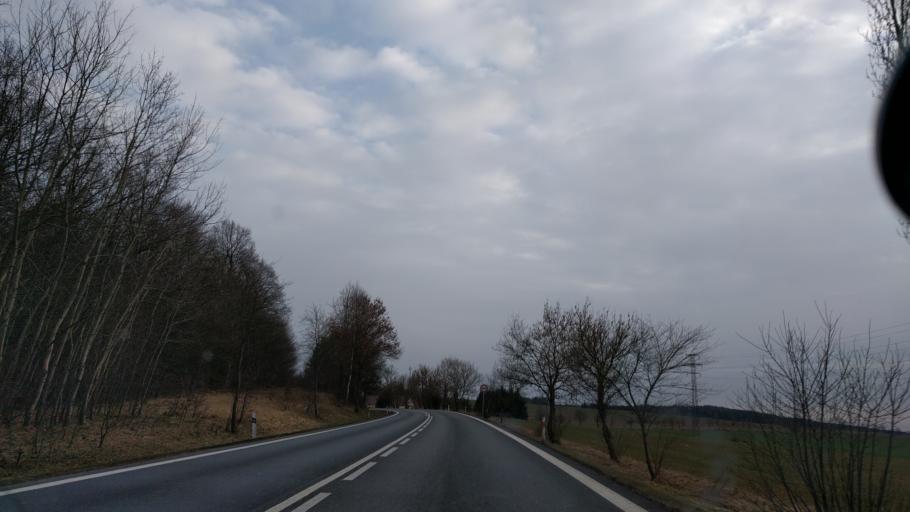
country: CZ
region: Central Bohemia
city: Milin
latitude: 49.5859
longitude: 14.0711
